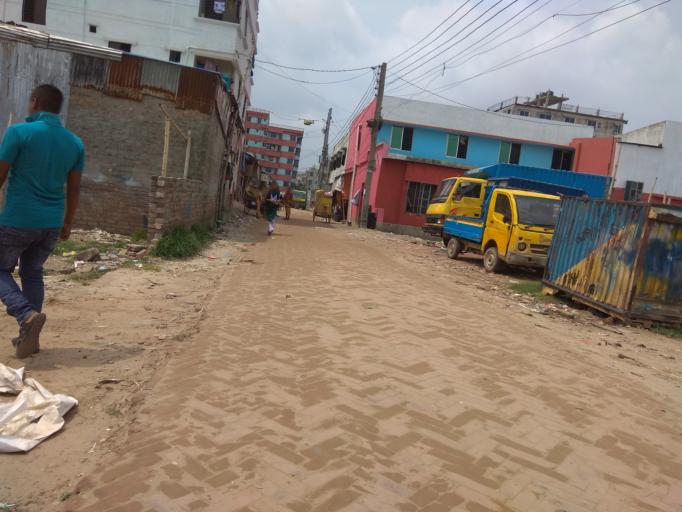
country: BD
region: Dhaka
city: Tungi
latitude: 23.8272
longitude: 90.3538
